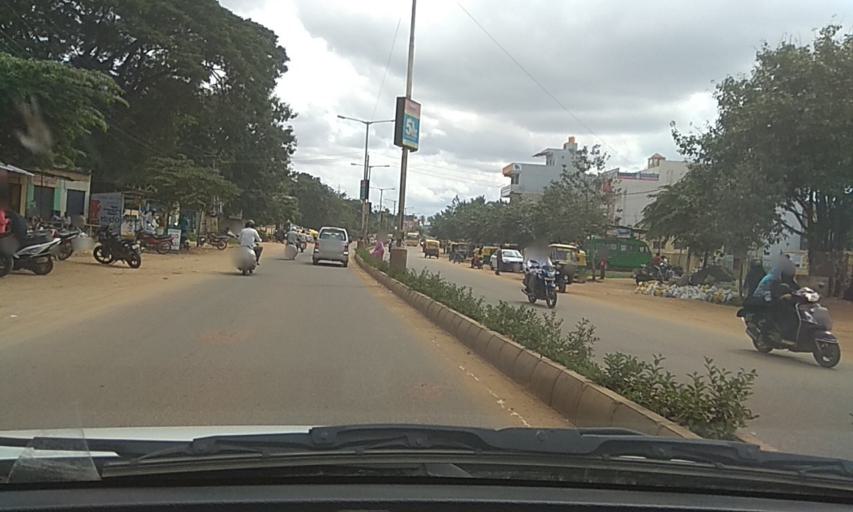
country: IN
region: Karnataka
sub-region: Tumkur
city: Tumkur
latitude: 13.3321
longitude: 77.0957
